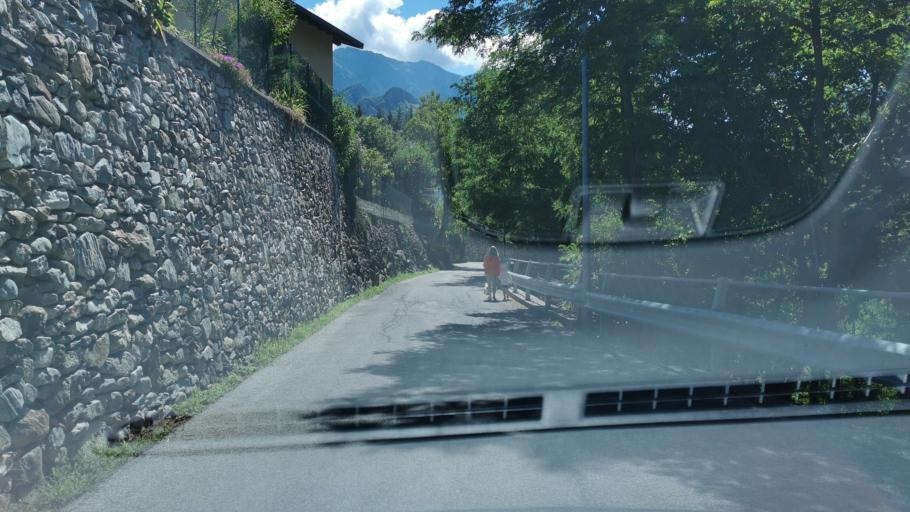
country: IT
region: Piedmont
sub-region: Provincia di Cuneo
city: Entracque
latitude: 44.2368
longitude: 7.3960
